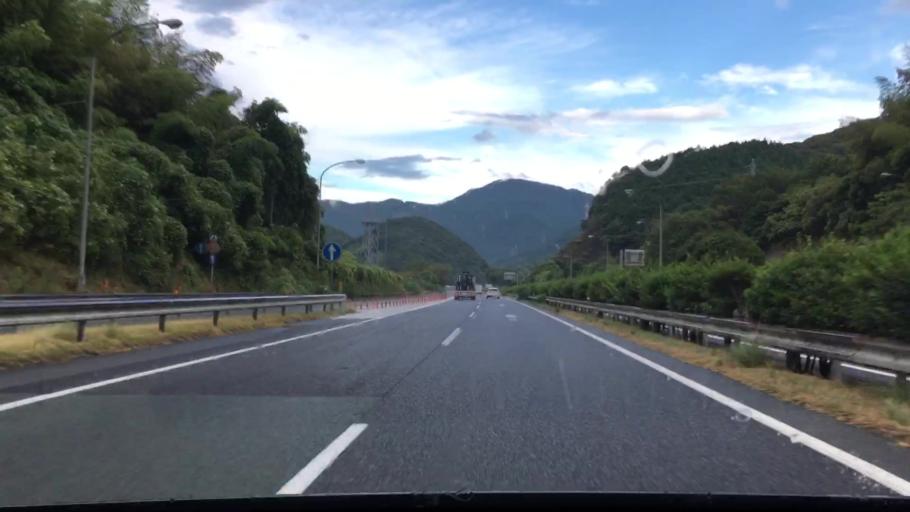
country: JP
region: Fukuoka
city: Kitakyushu
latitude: 33.8032
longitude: 130.8544
